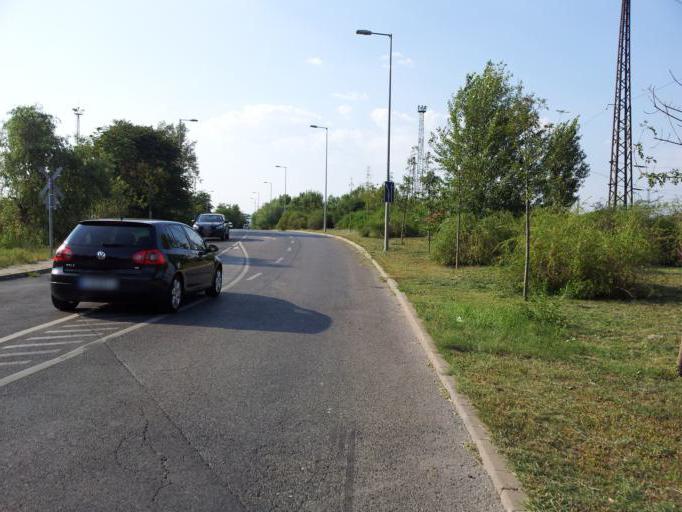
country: HU
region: Budapest
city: Budapest XX. keruelet
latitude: 47.4581
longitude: 19.0951
